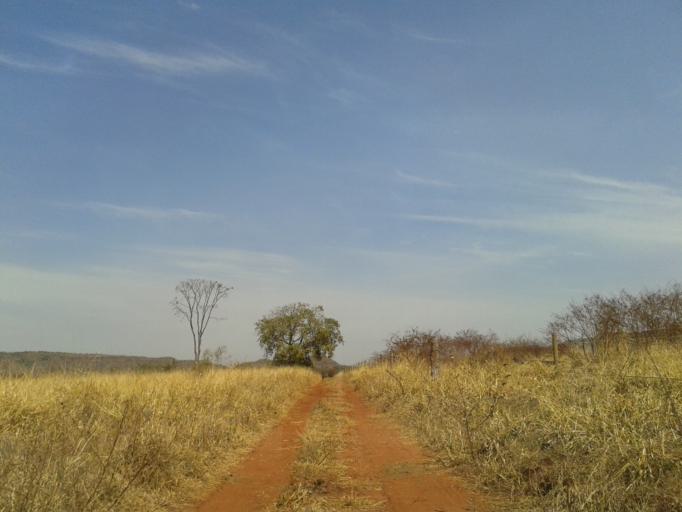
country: BR
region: Minas Gerais
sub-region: Santa Vitoria
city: Santa Vitoria
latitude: -19.2038
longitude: -50.0341
